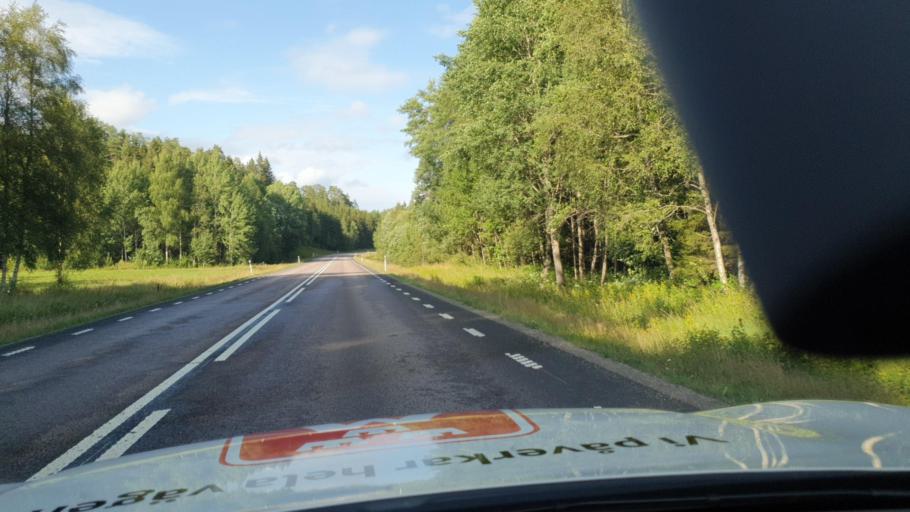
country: SE
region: Vaestra Goetaland
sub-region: Dals-Ed Kommun
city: Ed
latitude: 58.9059
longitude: 11.9995
